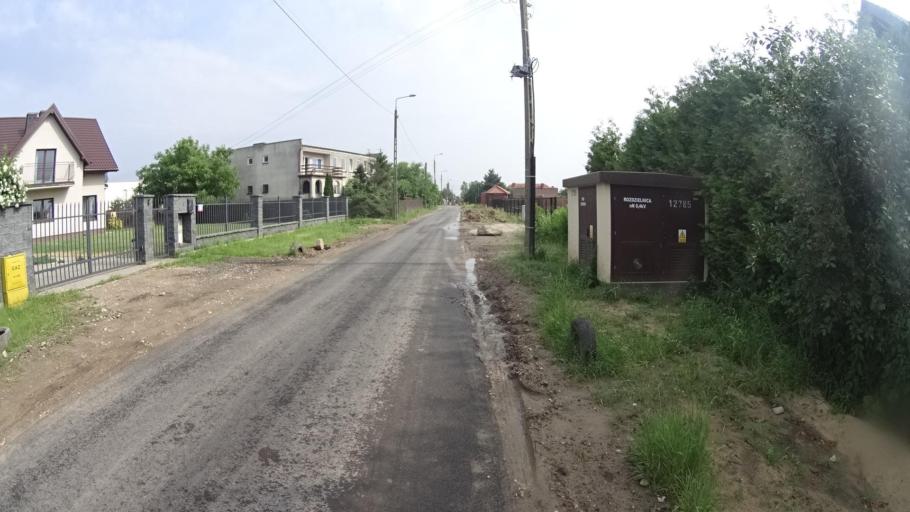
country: PL
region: Masovian Voivodeship
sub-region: Powiat pruszkowski
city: Raszyn
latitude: 52.1659
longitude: 20.9199
